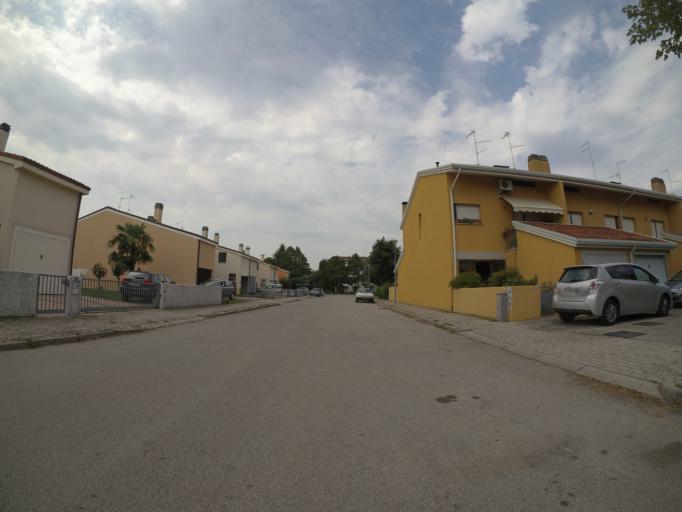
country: IT
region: Friuli Venezia Giulia
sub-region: Provincia di Udine
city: Codroipo
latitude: 45.9559
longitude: 12.9955
